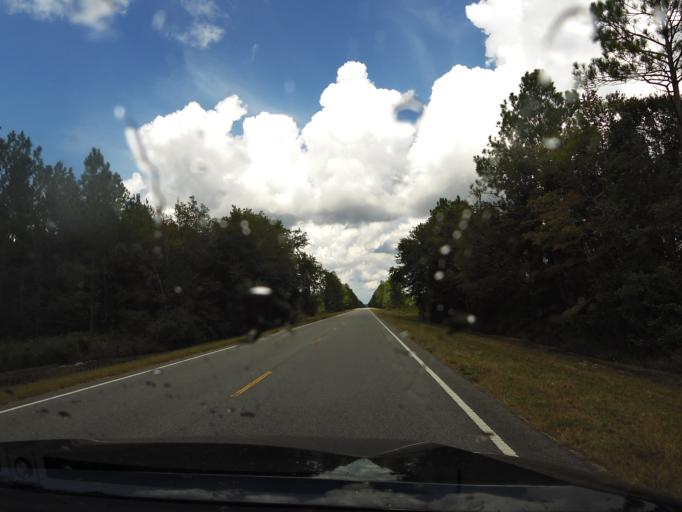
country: US
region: Georgia
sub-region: Charlton County
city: Folkston
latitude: 30.9019
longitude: -82.0174
